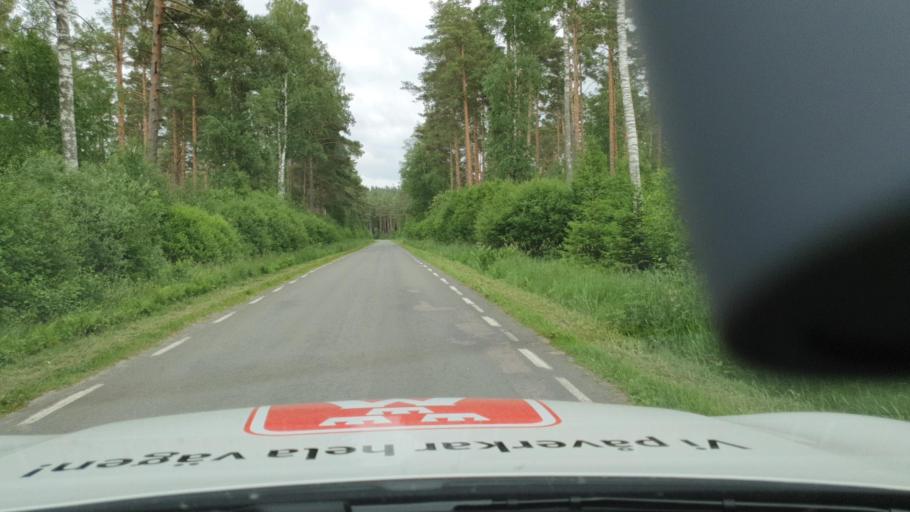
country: SE
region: Vaestra Goetaland
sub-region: Tidaholms Kommun
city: Olofstorp
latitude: 58.1900
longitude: 14.0832
